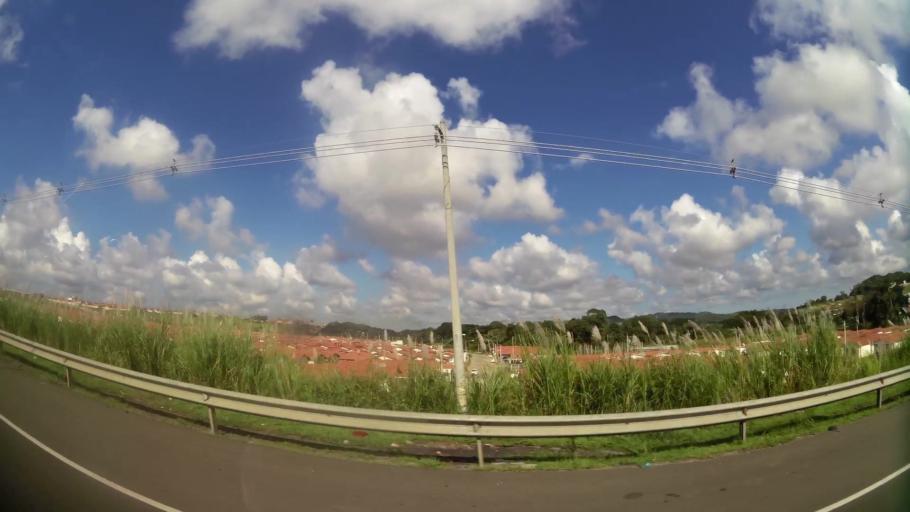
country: PA
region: Panama
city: Nuevo Arraijan
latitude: 8.9036
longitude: -79.7385
